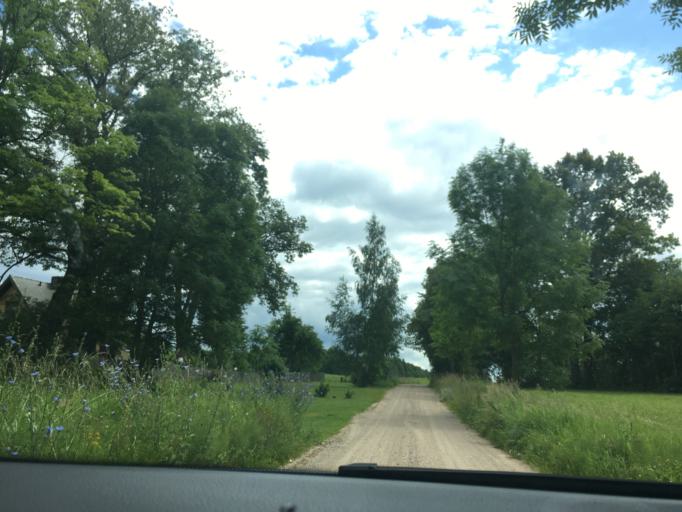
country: PL
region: Podlasie
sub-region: Powiat sejnenski
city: Krasnopol
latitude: 54.0972
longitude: 23.2709
